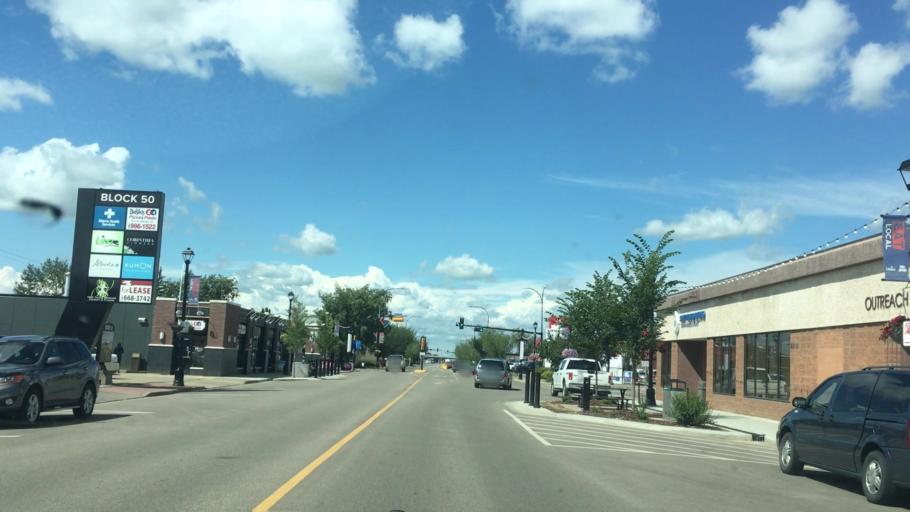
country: CA
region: Alberta
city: Leduc
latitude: 53.2648
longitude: -113.5507
